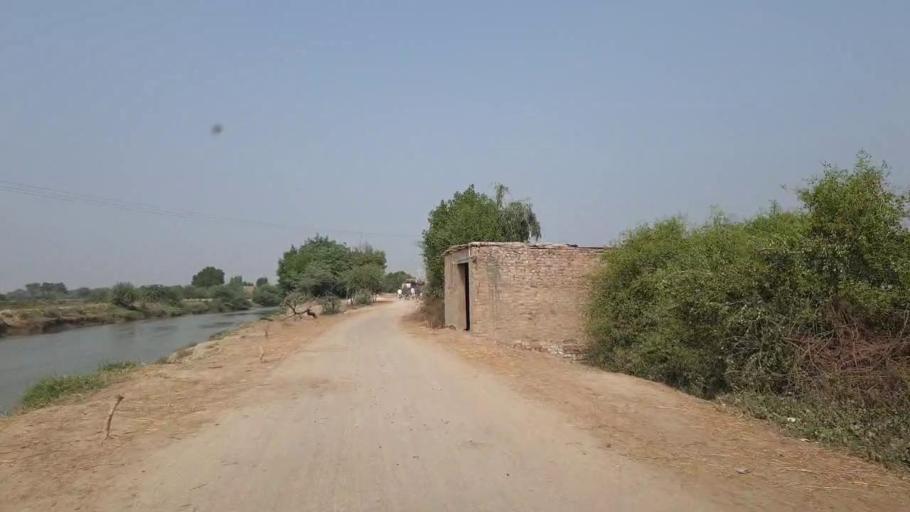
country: PK
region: Sindh
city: Kario
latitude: 24.9234
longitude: 68.6010
